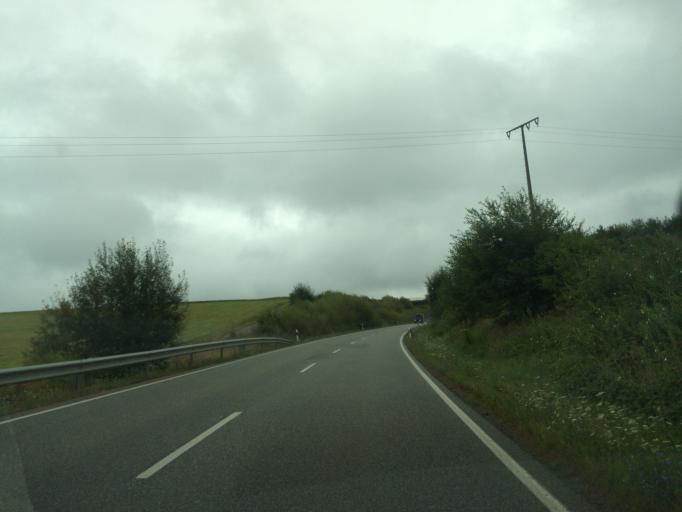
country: DE
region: Rheinland-Pfalz
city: Petersberg
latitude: 49.2078
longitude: 7.5719
